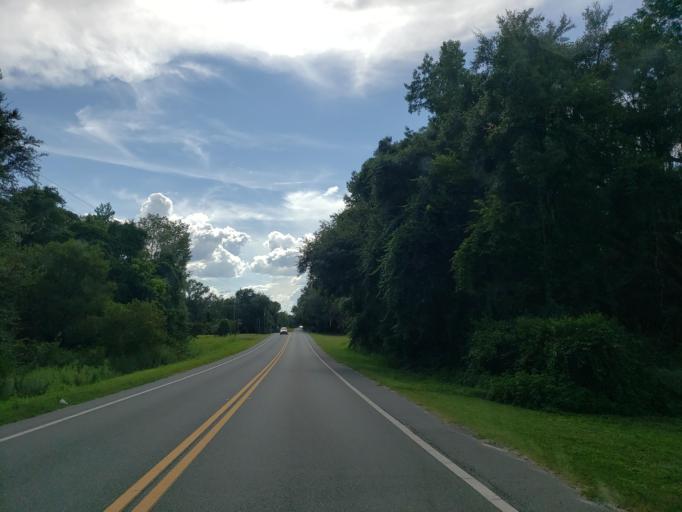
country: US
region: Georgia
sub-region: Echols County
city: Statenville
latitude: 30.5810
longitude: -83.2140
